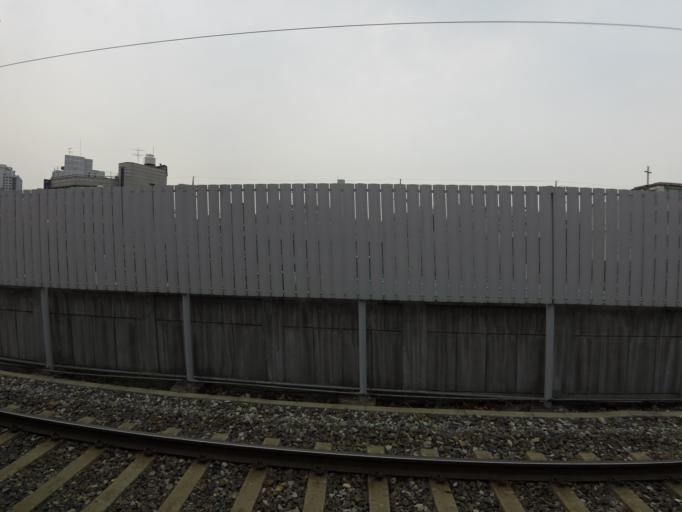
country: KR
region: Seoul
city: Seoul
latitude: 37.5423
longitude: 126.9711
